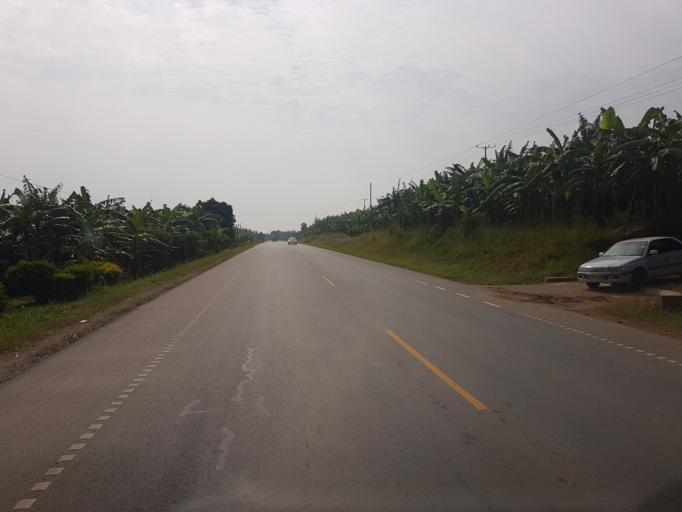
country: UG
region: Western Region
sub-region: Sheema District
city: Kibingo
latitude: -0.6372
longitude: 30.5152
